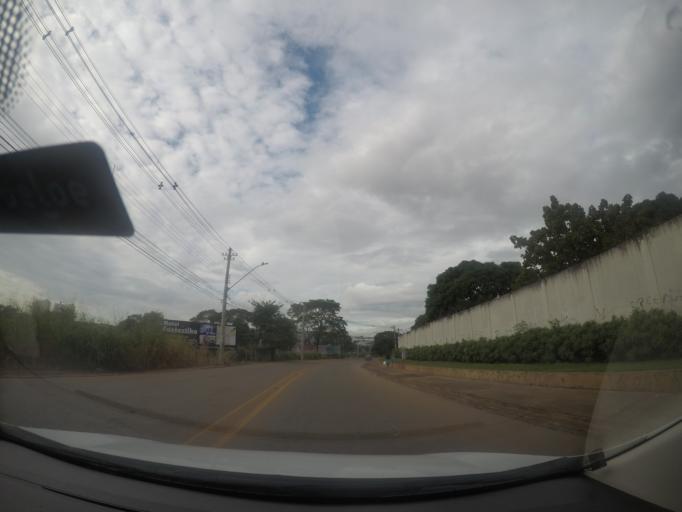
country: BR
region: Goias
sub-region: Goiania
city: Goiania
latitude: -16.6368
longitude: -49.3312
